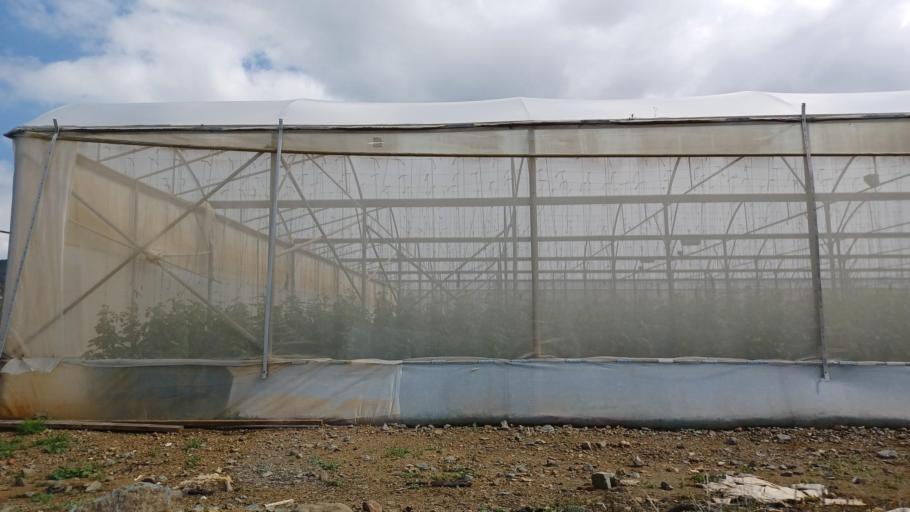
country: CY
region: Pafos
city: Polis
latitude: 35.1160
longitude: 32.5172
